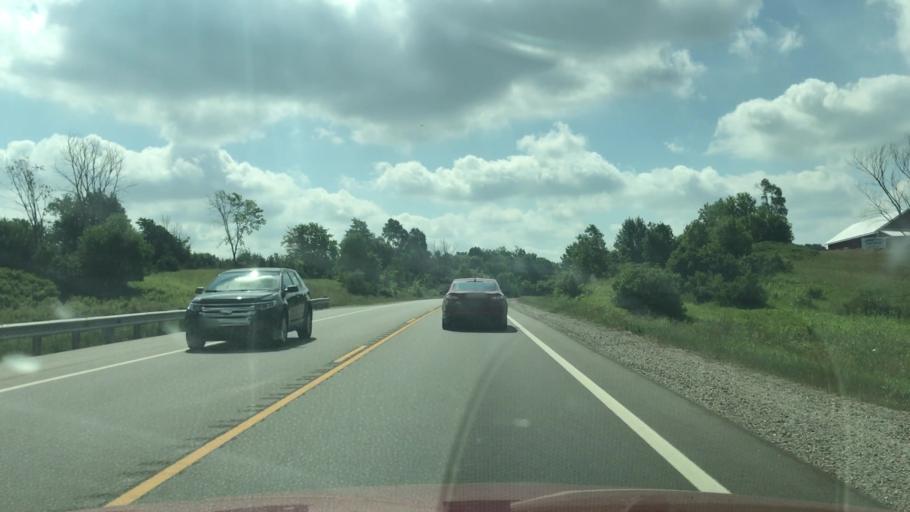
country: US
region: Michigan
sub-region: Kent County
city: Kent City
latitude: 43.1999
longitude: -85.7278
